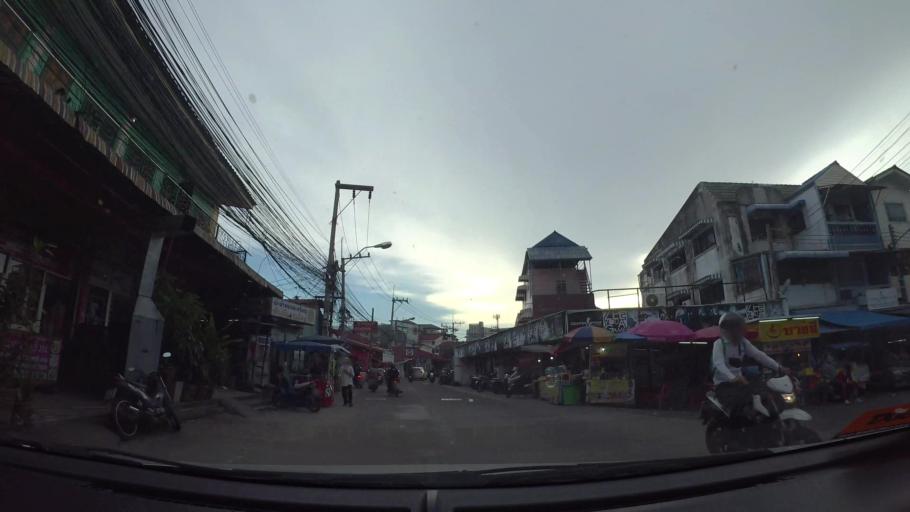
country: TH
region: Chon Buri
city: Phatthaya
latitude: 12.9195
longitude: 100.8826
